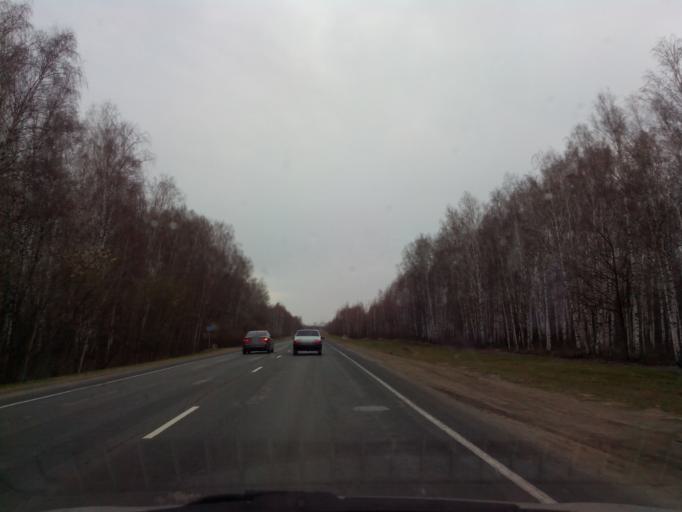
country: RU
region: Tambov
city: Michurinsk
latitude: 53.0744
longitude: 40.4239
